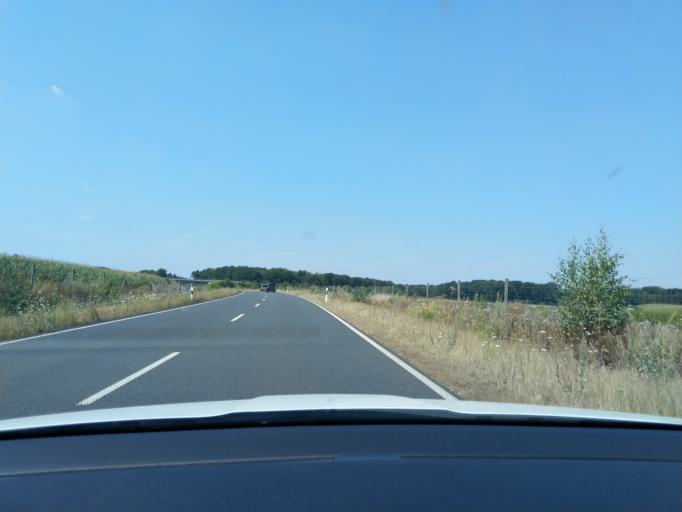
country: DE
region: North Rhine-Westphalia
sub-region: Regierungsbezirk Koln
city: Wassenberg
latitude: 51.1241
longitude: 6.2011
